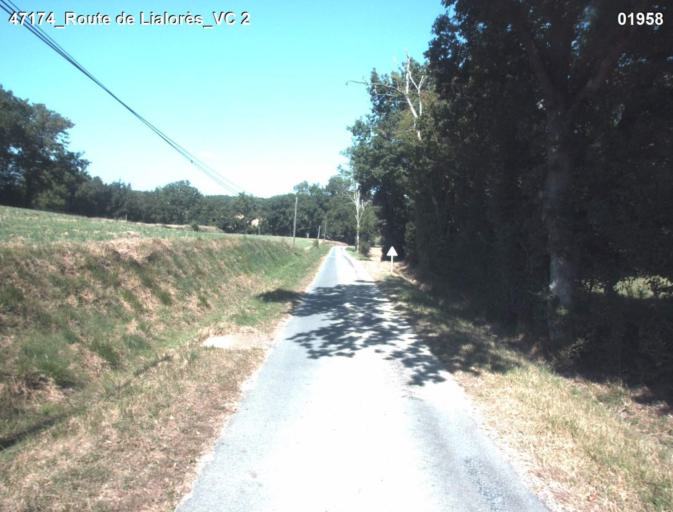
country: FR
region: Midi-Pyrenees
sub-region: Departement du Gers
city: Condom
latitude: 44.0214
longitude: 0.3707
